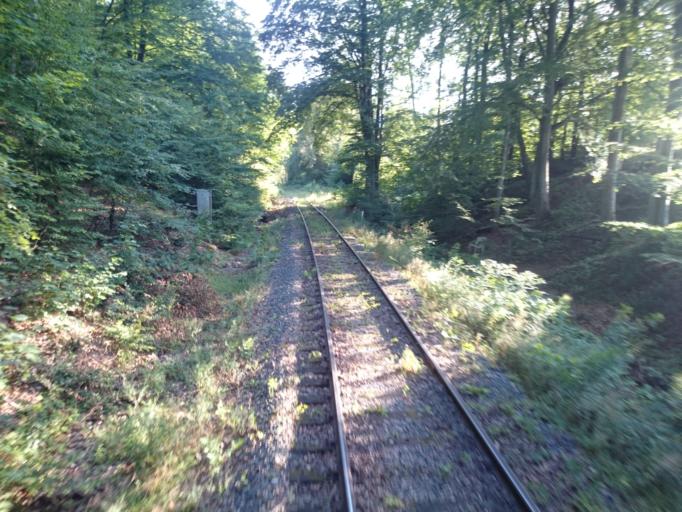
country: SE
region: Skane
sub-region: Simrishamns Kommun
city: Kivik
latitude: 55.6727
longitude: 14.1480
